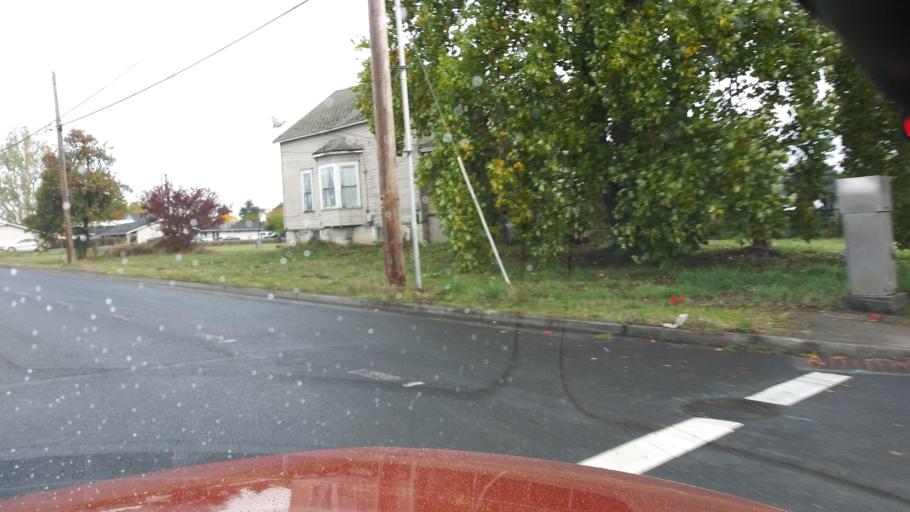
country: US
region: Oregon
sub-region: Washington County
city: Cornelius
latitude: 45.5201
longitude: -123.0668
